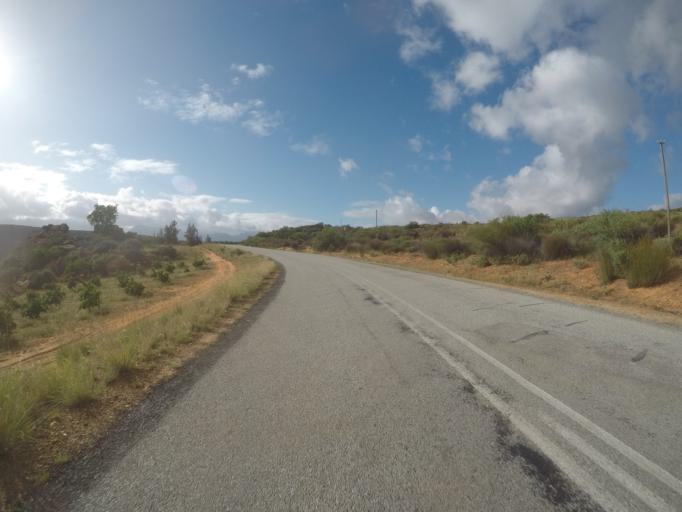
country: ZA
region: Western Cape
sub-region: West Coast District Municipality
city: Clanwilliam
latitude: -32.4252
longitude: 18.9349
